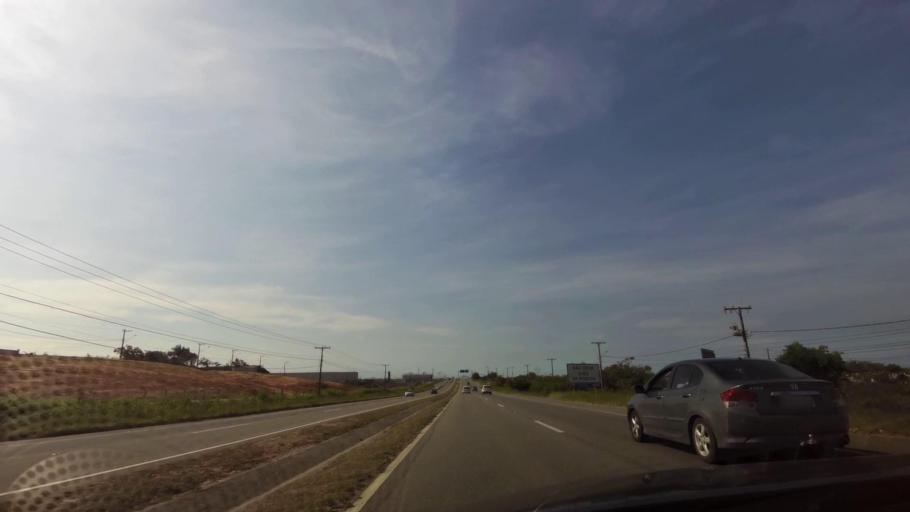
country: BR
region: Espirito Santo
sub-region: Viana
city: Viana
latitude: -20.4930
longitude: -40.3558
